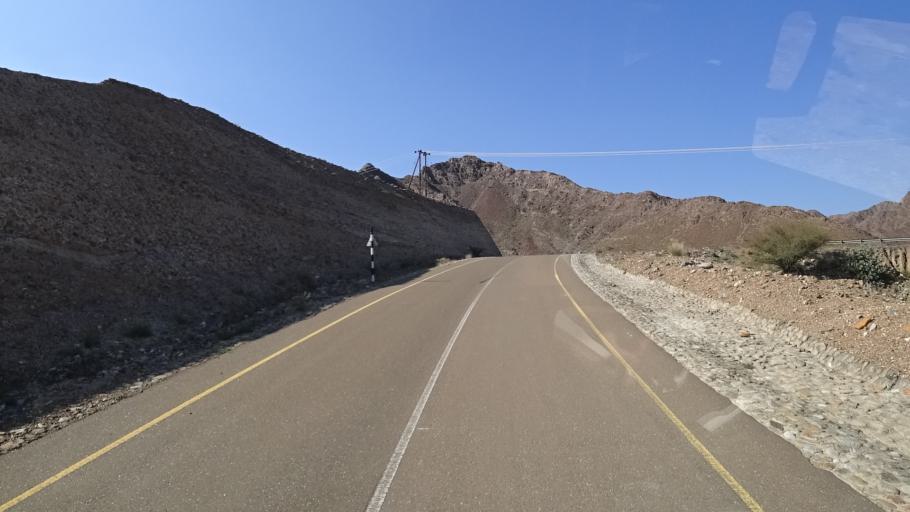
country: OM
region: Al Batinah
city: Rustaq
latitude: 23.4588
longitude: 57.0822
